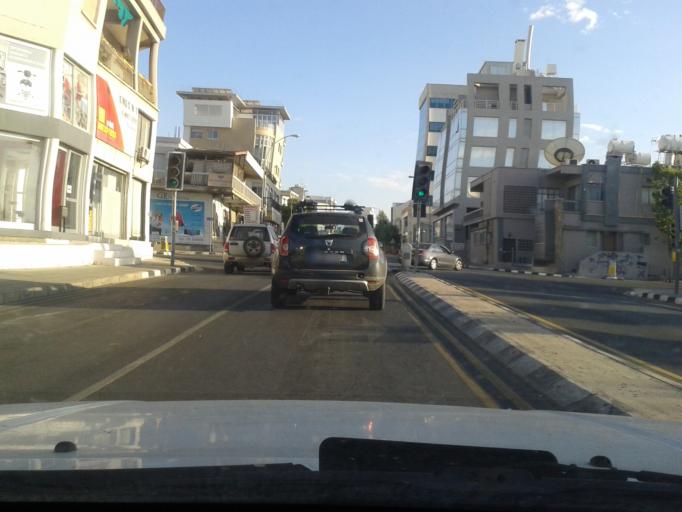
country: CY
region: Lefkosia
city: Nicosia
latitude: 35.1519
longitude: 33.3594
